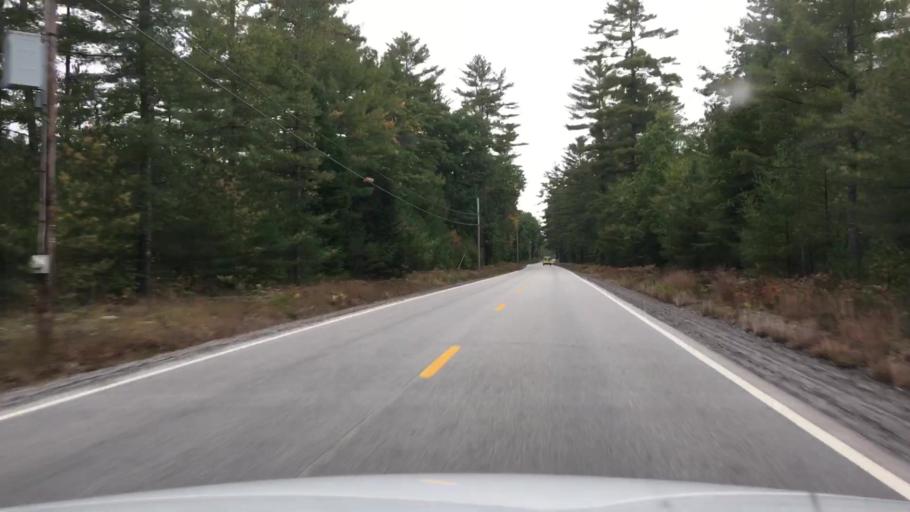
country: US
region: Maine
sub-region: Cumberland County
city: Harrison
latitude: 44.2197
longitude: -70.6906
